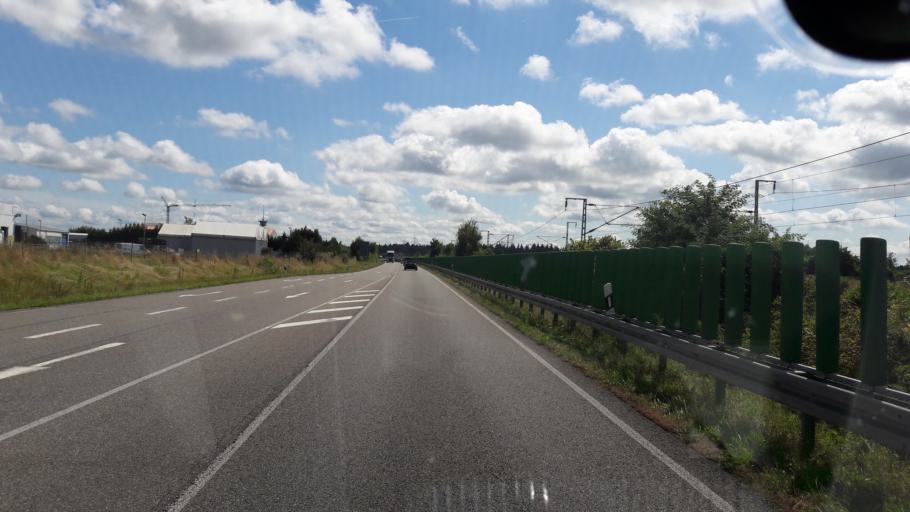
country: DE
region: Baden-Wuerttemberg
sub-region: Karlsruhe Region
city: Waghausel
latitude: 49.2480
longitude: 8.4992
